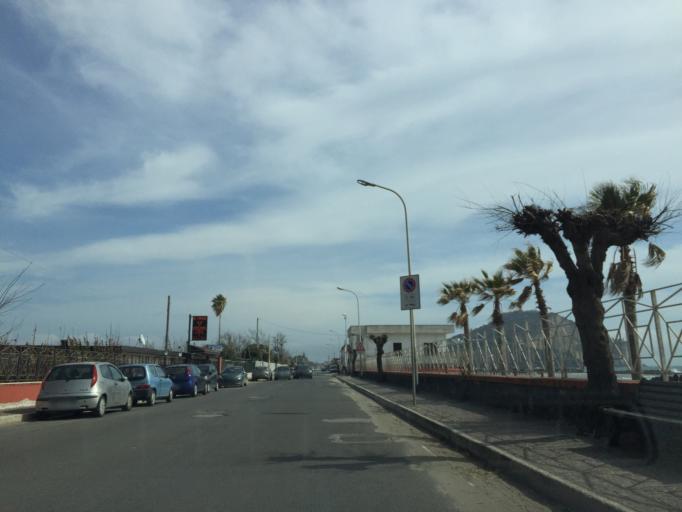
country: IT
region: Campania
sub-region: Provincia di Napoli
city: Bacoli
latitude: 40.7891
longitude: 14.0679
